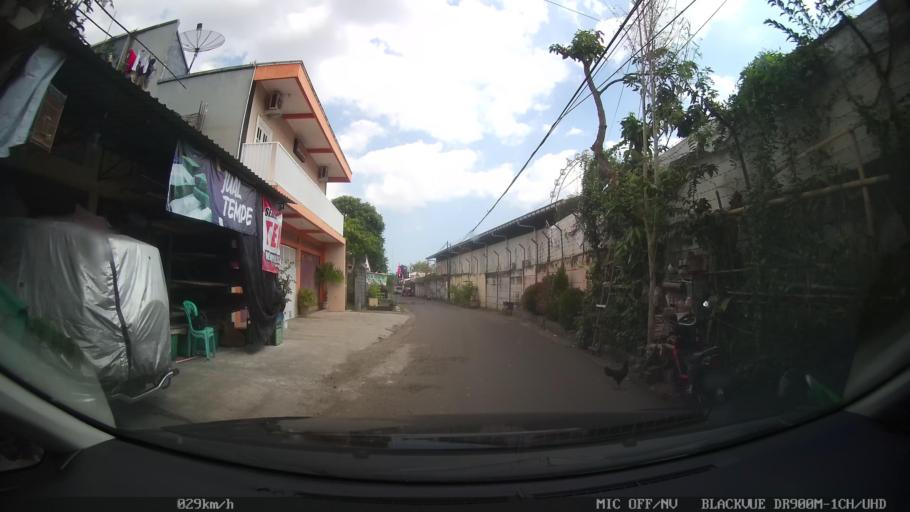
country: ID
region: Daerah Istimewa Yogyakarta
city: Yogyakarta
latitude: -7.7662
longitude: 110.3562
